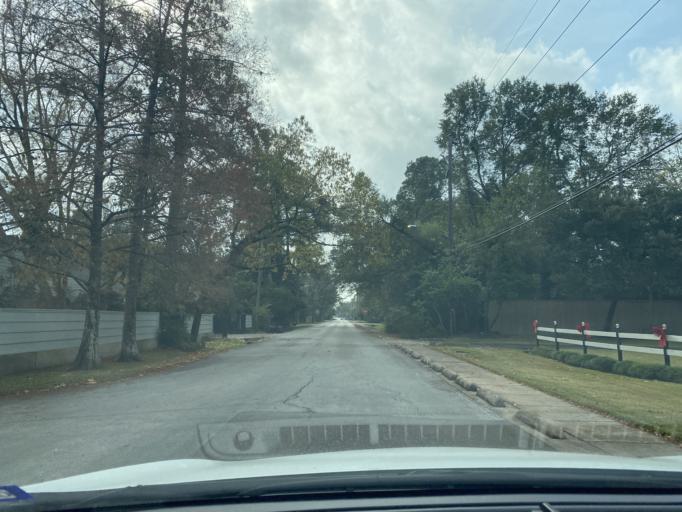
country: US
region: Texas
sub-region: Harris County
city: Hunters Creek Village
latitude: 29.7672
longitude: -95.4677
